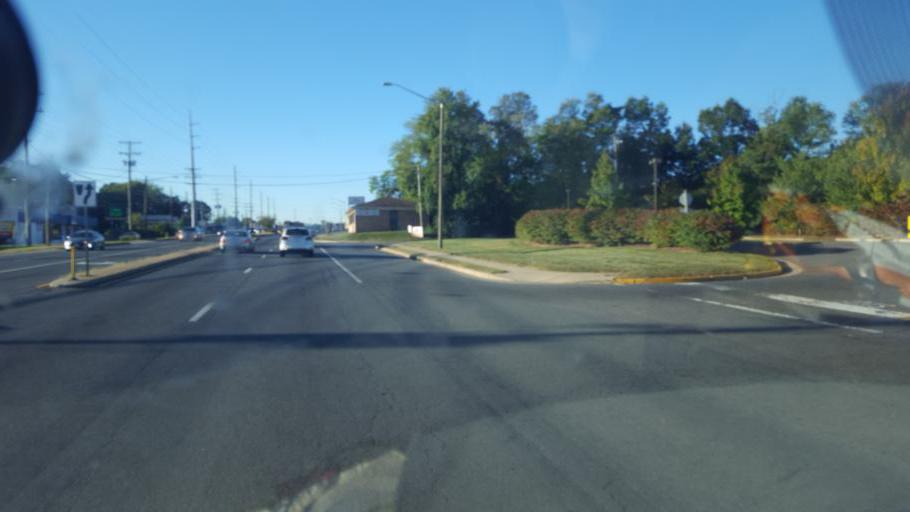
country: US
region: Virginia
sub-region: Prince William County
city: Yorkshire
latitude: 38.7752
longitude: -77.4518
